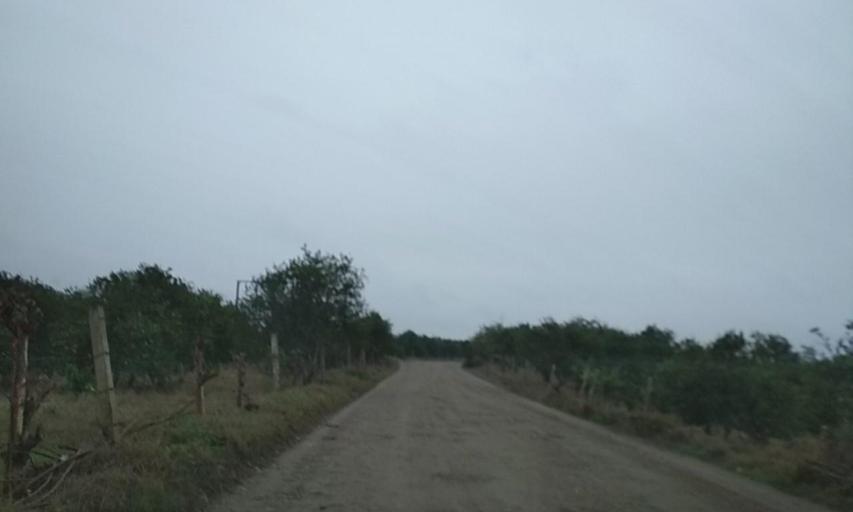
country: MX
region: Veracruz
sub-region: Papantla
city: El Chote
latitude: 20.3379
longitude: -97.3902
